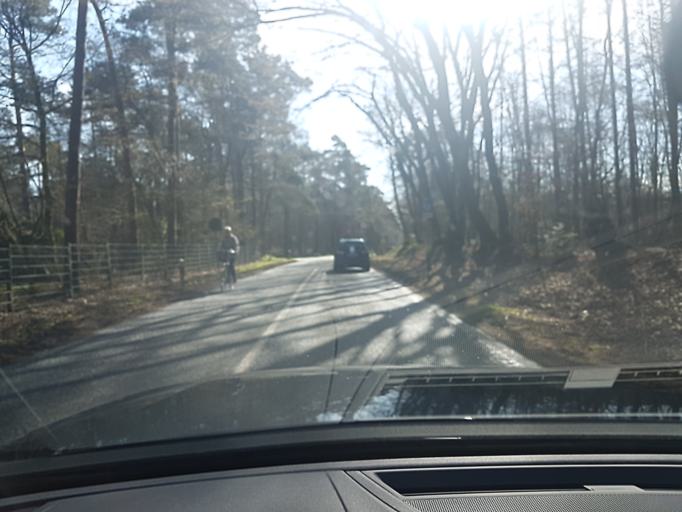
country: DE
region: North Rhine-Westphalia
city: Oer-Erkenschwick
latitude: 51.7288
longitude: 7.2825
